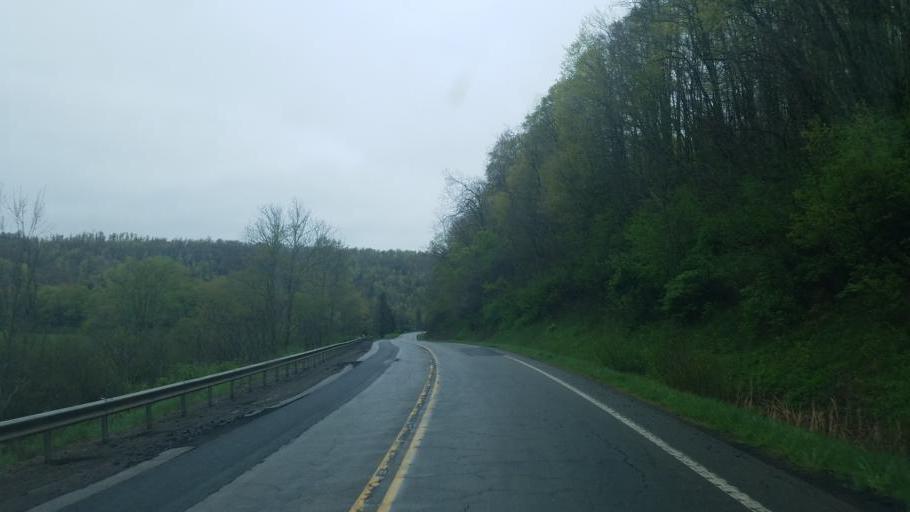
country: US
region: Pennsylvania
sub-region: Potter County
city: Coudersport
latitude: 41.8163
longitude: -77.9883
